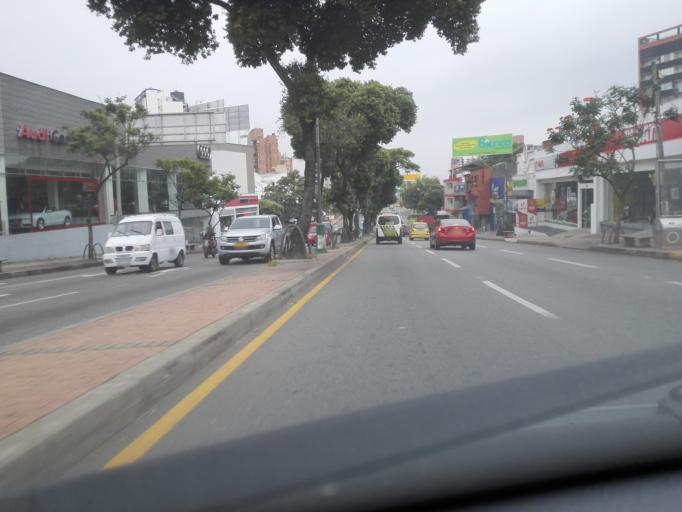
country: CO
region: Santander
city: Bucaramanga
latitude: 7.1132
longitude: -73.1148
